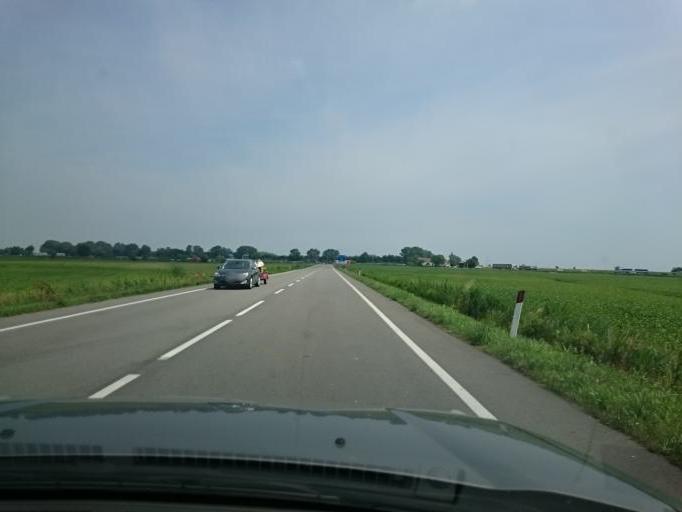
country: IT
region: Veneto
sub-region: Provincia di Padova
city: Codevigo
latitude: 45.2504
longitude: 12.1285
